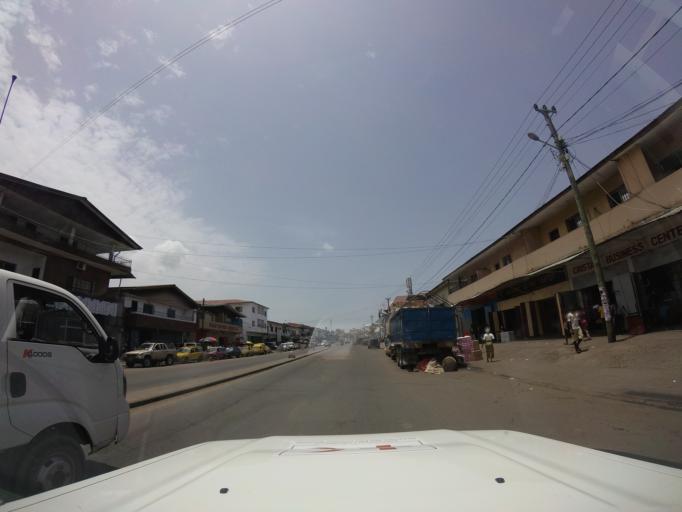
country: LR
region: Montserrado
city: Monrovia
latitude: 6.3264
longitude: -10.8010
